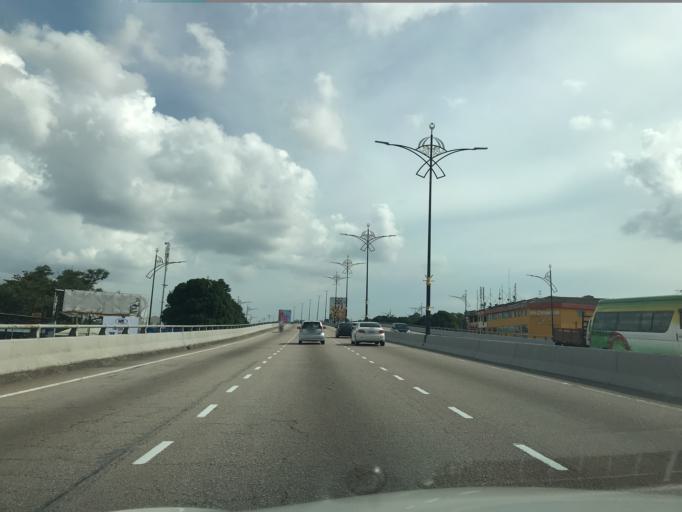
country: MY
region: Johor
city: Skudai
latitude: 1.5334
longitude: 103.6662
